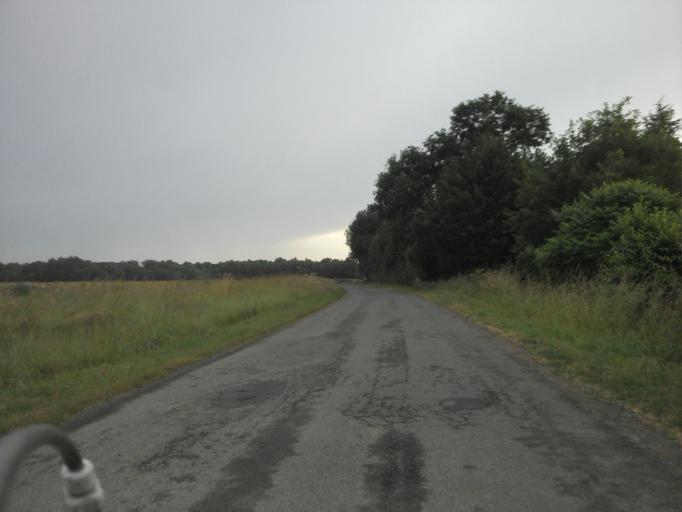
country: FR
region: Pays de la Loire
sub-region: Departement de Maine-et-Loire
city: Breze
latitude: 47.1046
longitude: -0.0050
